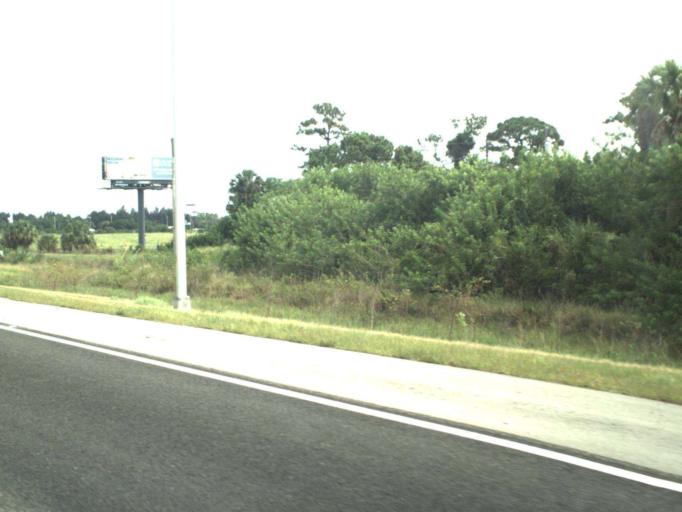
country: US
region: Florida
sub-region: Saint Lucie County
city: Lakewood Park
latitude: 27.4394
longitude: -80.3903
